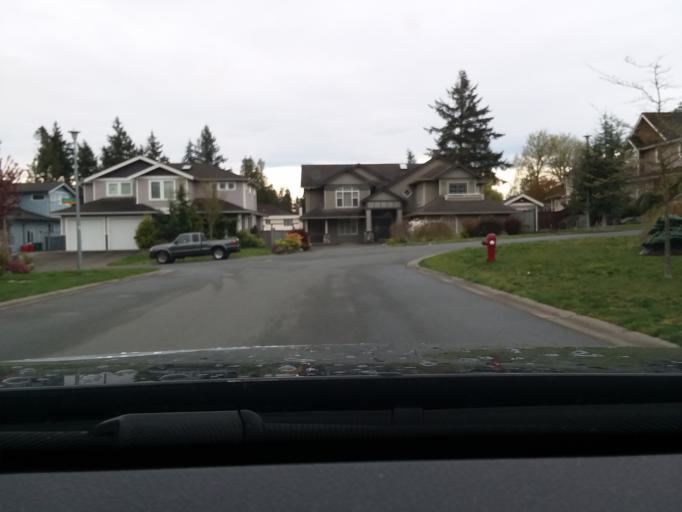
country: CA
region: British Columbia
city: Victoria
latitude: 48.5175
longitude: -123.3803
